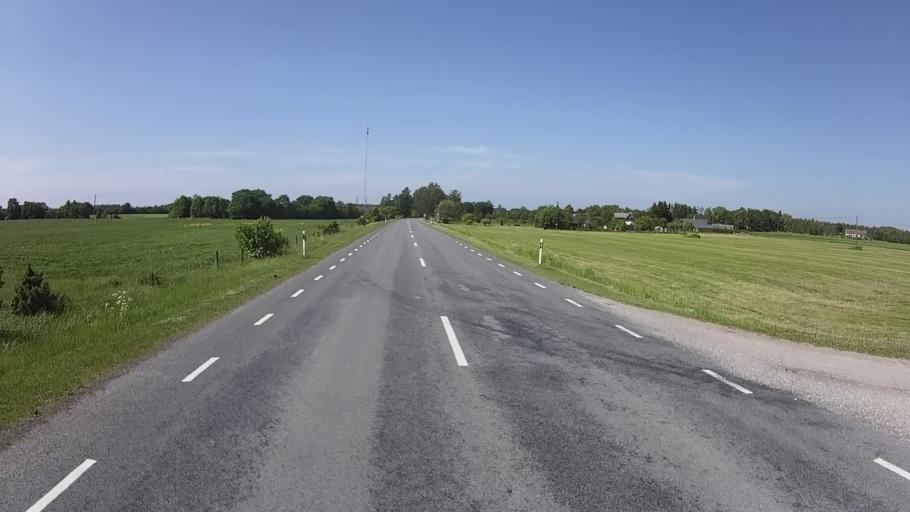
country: EE
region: Saare
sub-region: Kuressaare linn
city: Kuressaare
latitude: 58.3316
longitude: 22.4558
